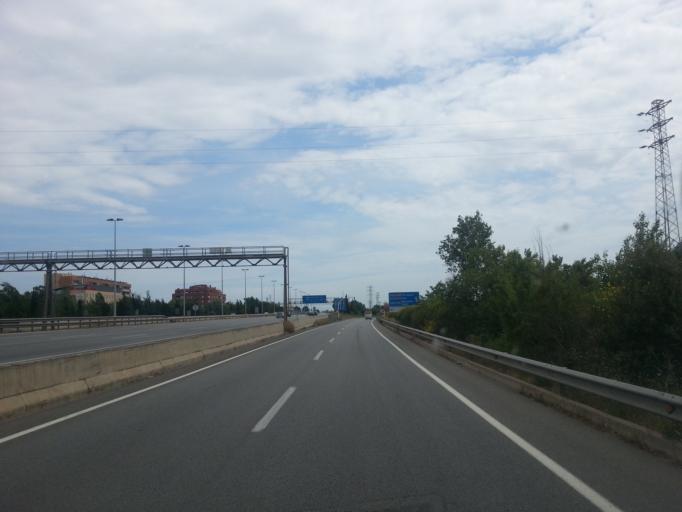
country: ES
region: Catalonia
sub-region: Provincia de Barcelona
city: Molins de Rei
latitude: 41.4169
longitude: 2.0097
